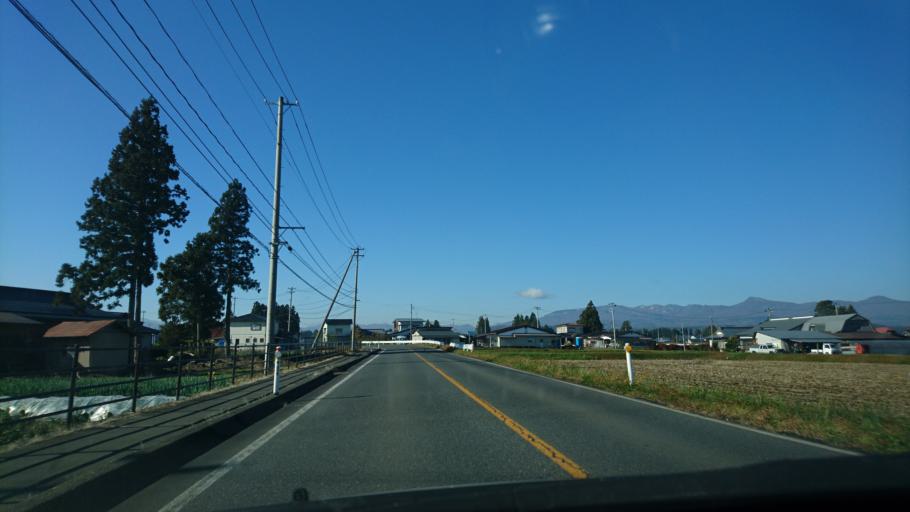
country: JP
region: Iwate
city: Mizusawa
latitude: 39.1374
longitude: 141.0713
